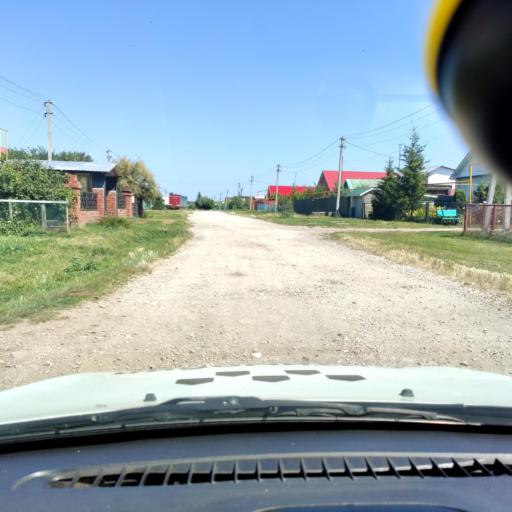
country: RU
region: Samara
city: Tol'yatti
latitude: 53.6386
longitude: 49.2911
